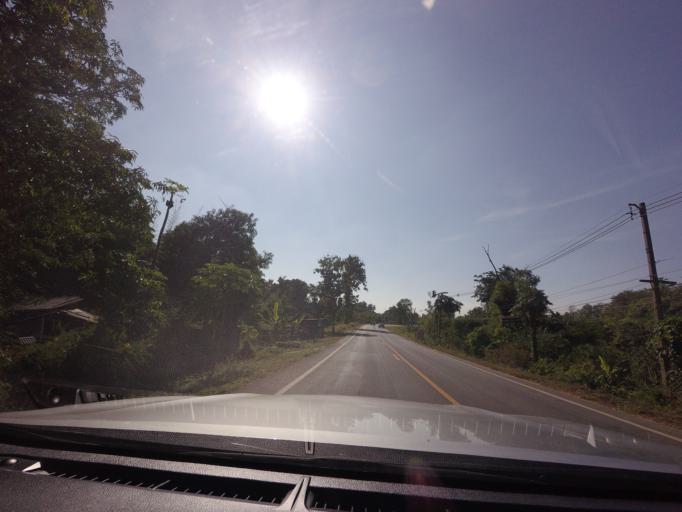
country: TH
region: Sukhothai
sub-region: Amphoe Si Satchanalai
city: Si Satchanalai
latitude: 17.6318
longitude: 99.6894
